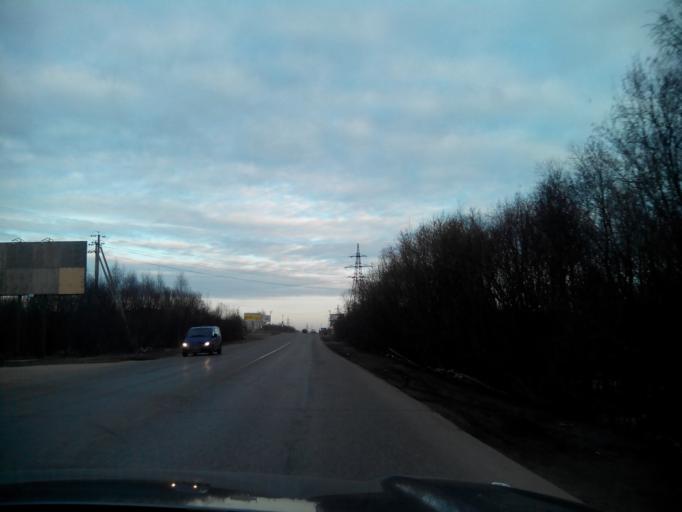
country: RU
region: Arkhangelskaya
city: Arkhangel'sk
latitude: 64.5210
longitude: 40.6728
